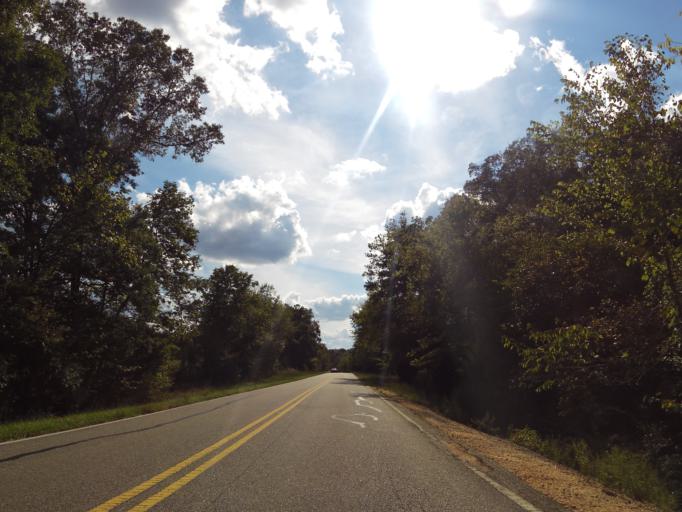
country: US
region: Alabama
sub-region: Dallas County
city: Selmont-West Selmont
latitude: 32.1816
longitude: -87.0432
